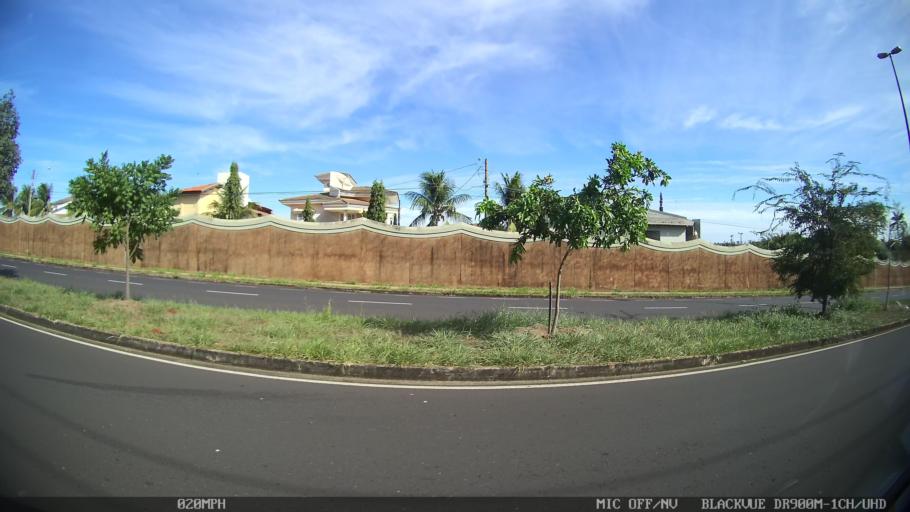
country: BR
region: Sao Paulo
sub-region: Sao Jose Do Rio Preto
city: Sao Jose do Rio Preto
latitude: -20.8092
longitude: -49.3432
